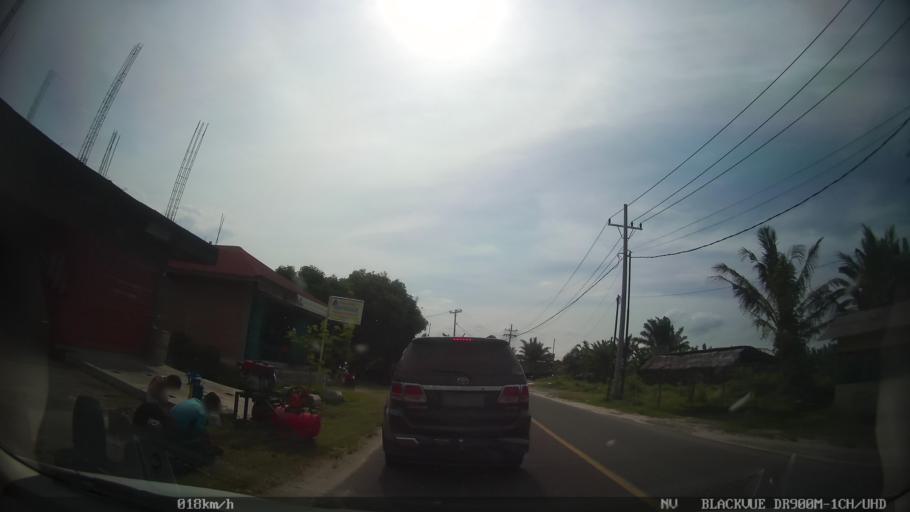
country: ID
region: North Sumatra
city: Percut
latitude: 3.6158
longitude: 98.8364
